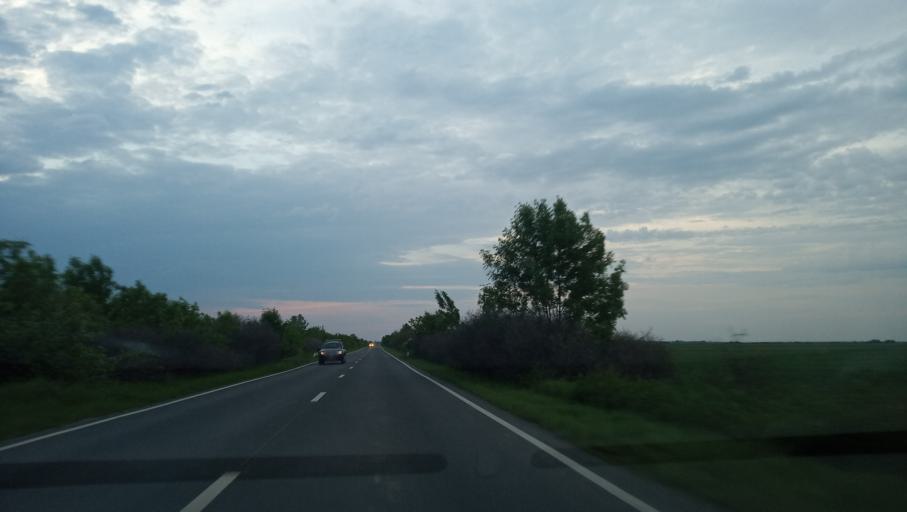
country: RO
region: Timis
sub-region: Comuna Jebel
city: Jebel
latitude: 45.5341
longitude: 21.2286
